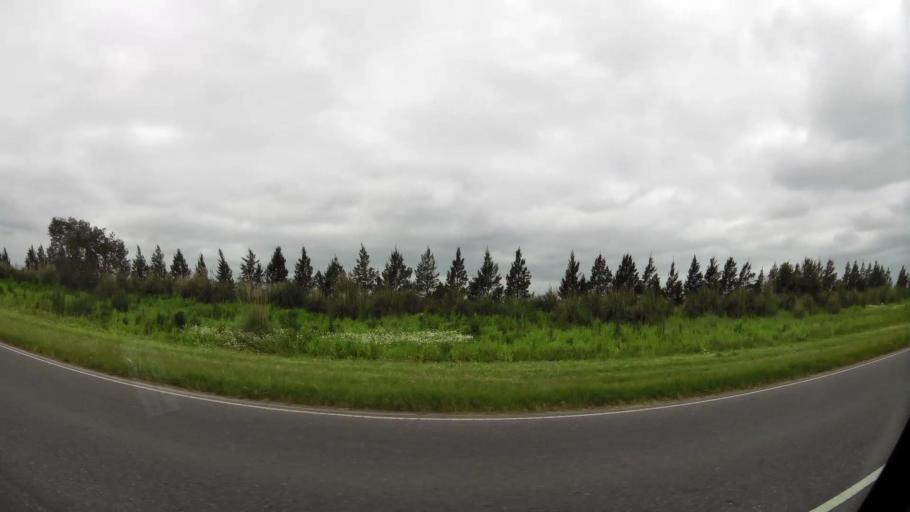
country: AR
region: Buenos Aires
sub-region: Partido de San Vicente
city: San Vicente
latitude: -35.0197
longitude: -58.4655
